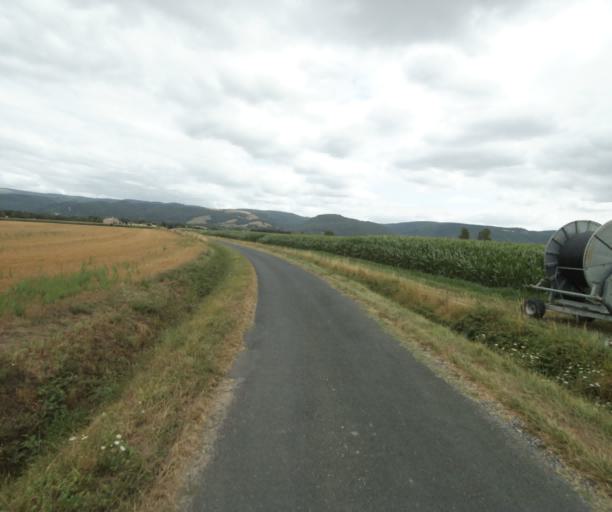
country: FR
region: Midi-Pyrenees
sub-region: Departement du Tarn
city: Soreze
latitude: 43.4745
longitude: 2.0500
